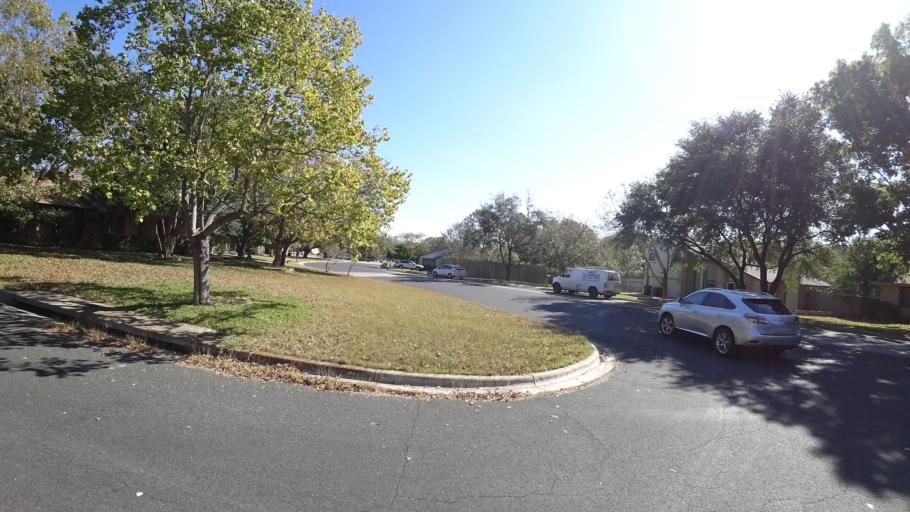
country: US
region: Texas
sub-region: Williamson County
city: Jollyville
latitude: 30.4212
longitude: -97.7642
